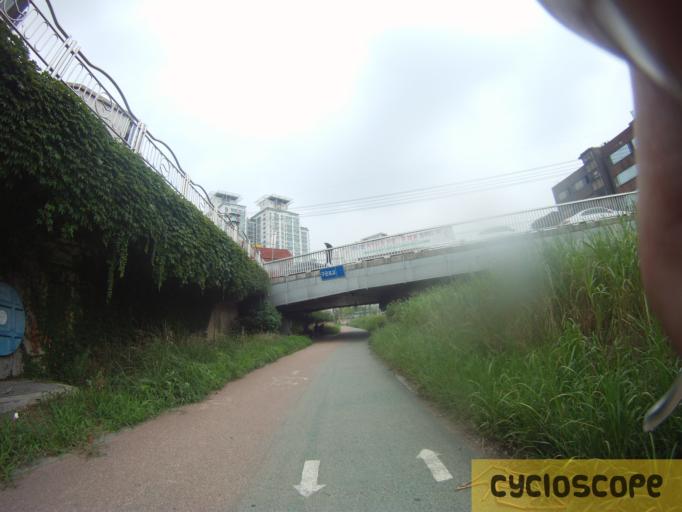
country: KR
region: Gyeonggi-do
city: Anyang-si
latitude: 37.3662
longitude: 126.9549
